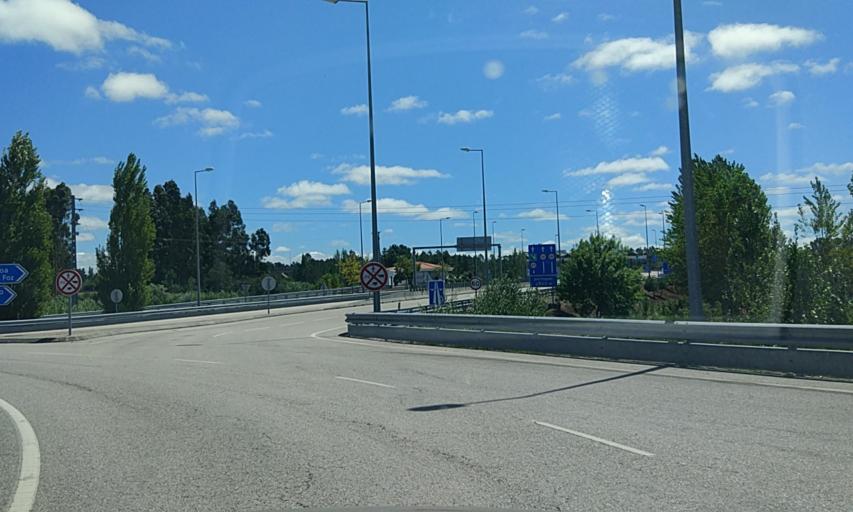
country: PT
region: Coimbra
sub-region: Montemor-O-Velho
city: Arazede
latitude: 40.3312
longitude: -8.7273
